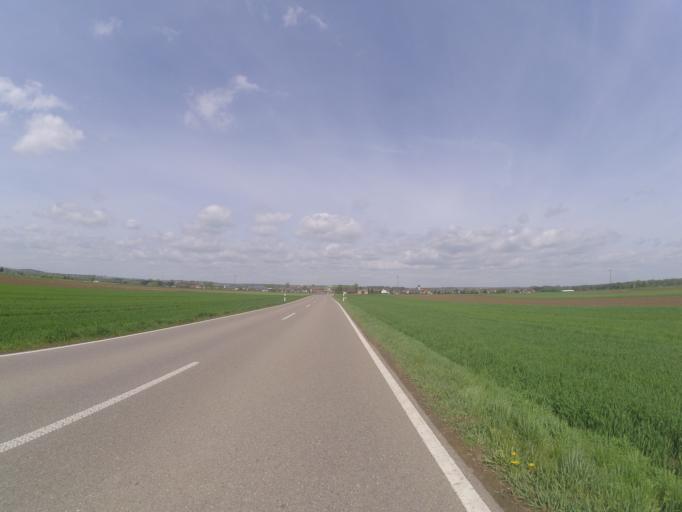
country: DE
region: Baden-Wuerttemberg
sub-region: Tuebingen Region
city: Ersingen
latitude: 48.2841
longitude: 9.8559
